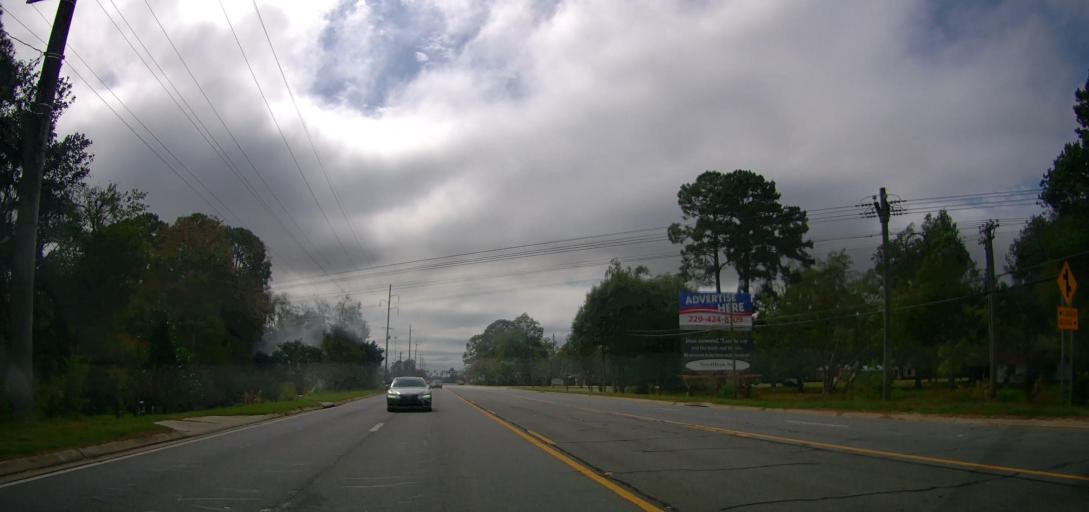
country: US
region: Georgia
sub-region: Colquitt County
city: Moultrie
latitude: 31.2114
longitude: -83.7757
